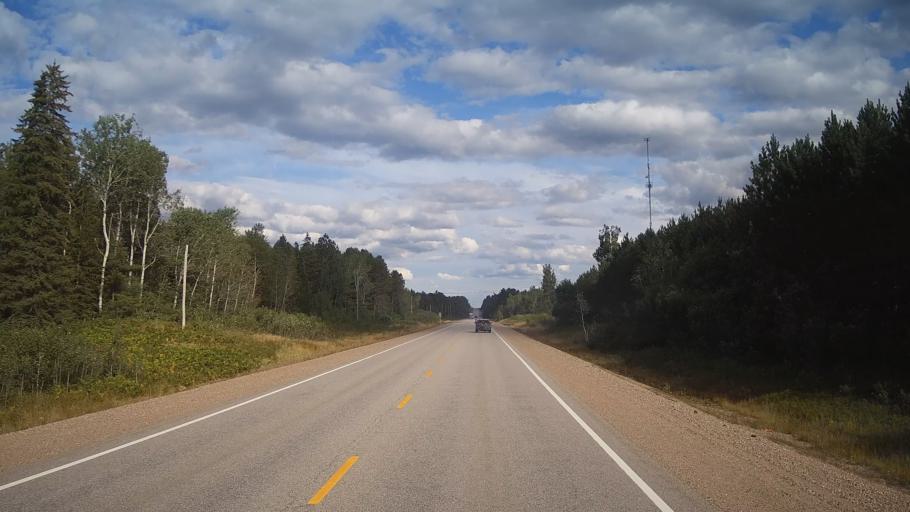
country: CA
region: Ontario
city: Mattawa
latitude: 46.2906
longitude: -78.5282
